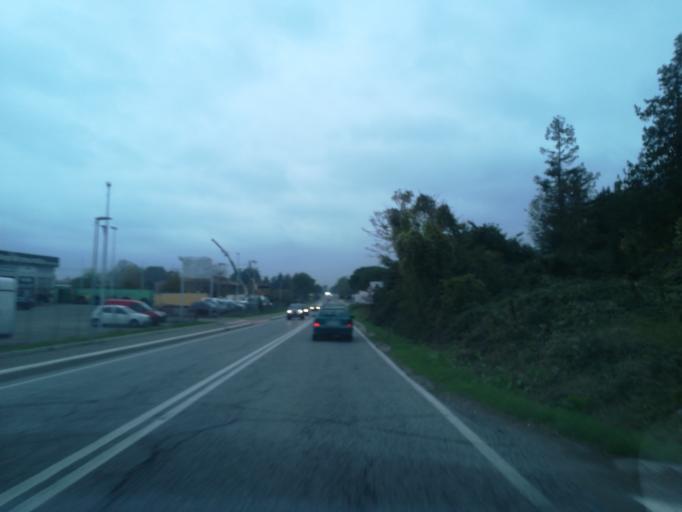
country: IT
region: Emilia-Romagna
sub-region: Provincia di Bologna
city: Toscanella
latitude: 44.3783
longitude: 11.6504
